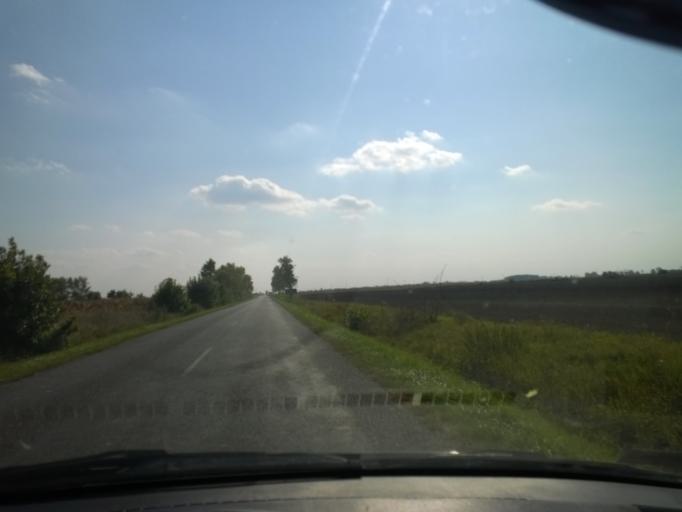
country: HU
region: Bacs-Kiskun
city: Kalocsa
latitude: 46.4965
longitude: 19.0524
